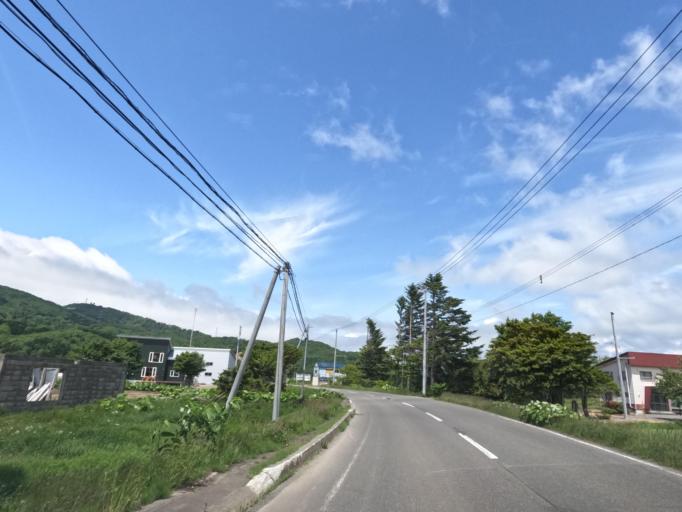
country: JP
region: Hokkaido
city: Tobetsu
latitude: 43.2870
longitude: 141.5379
